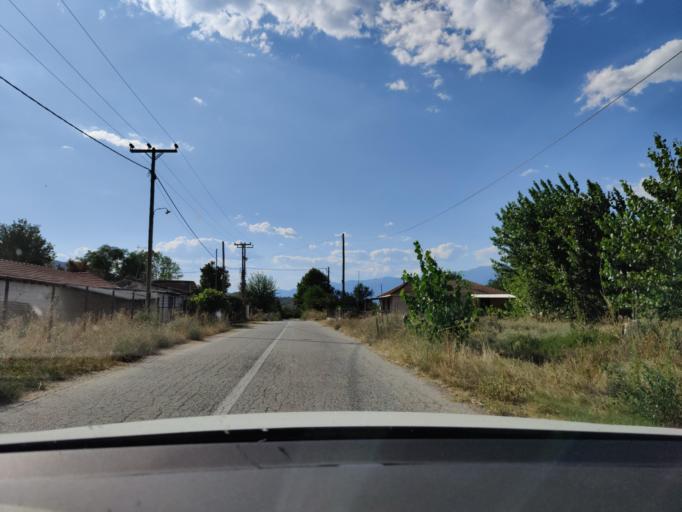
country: GR
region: Central Macedonia
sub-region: Nomos Serron
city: Chrysochorafa
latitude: 41.1810
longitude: 23.1078
